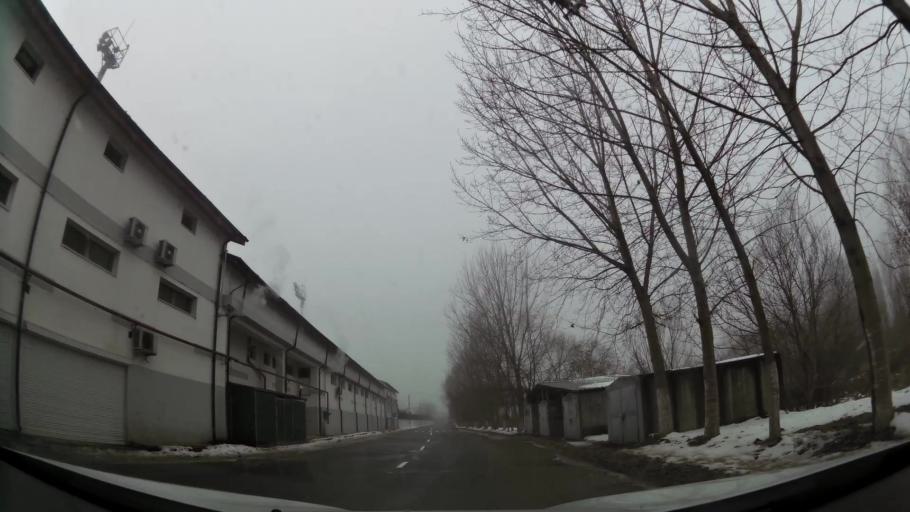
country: RO
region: Ilfov
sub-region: Comuna Chiajna
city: Chiajna
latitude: 44.4655
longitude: 25.9787
